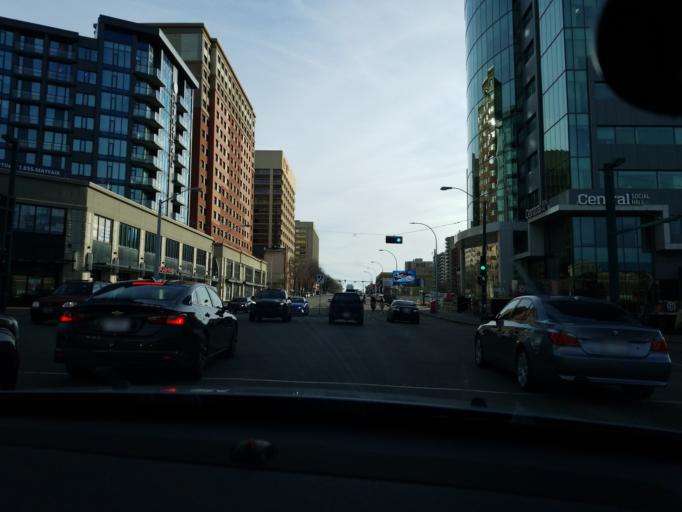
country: CA
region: Alberta
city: Edmonton
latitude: 53.5413
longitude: -113.5086
